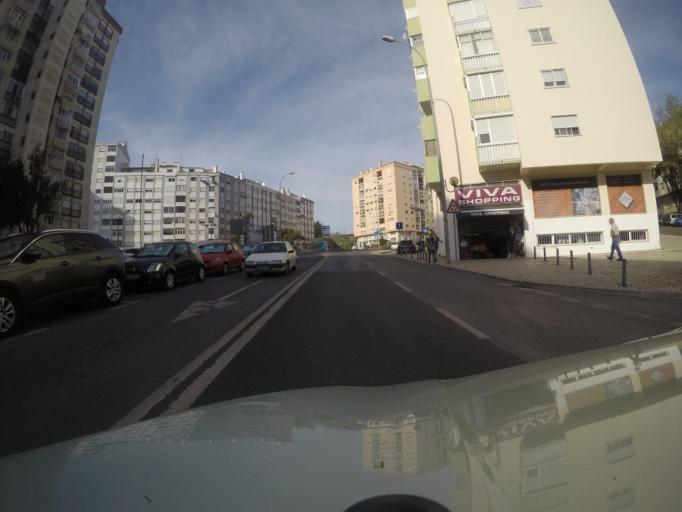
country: PT
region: Lisbon
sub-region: Amadora
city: Amadora
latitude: 38.7679
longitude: -9.2305
